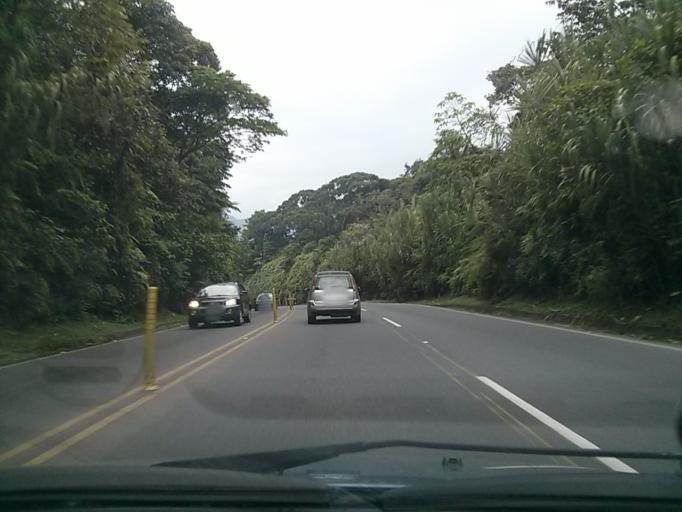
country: CR
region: San Jose
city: Dulce Nombre de Jesus
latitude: 10.1741
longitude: -83.9316
